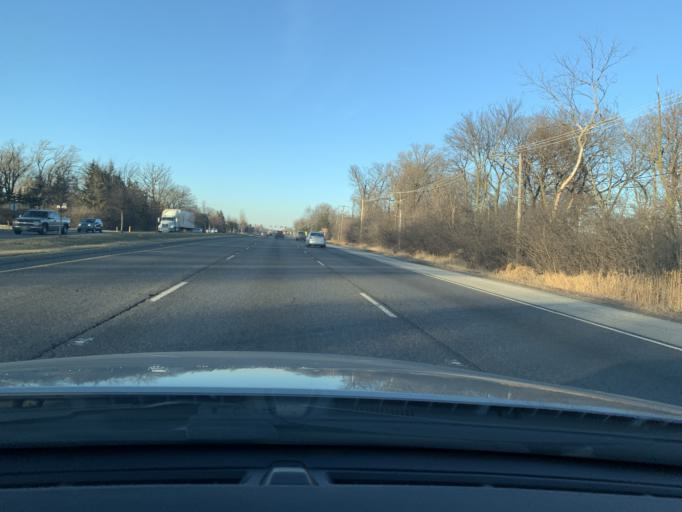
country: US
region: Illinois
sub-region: DuPage County
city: Bensenville
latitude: 41.9517
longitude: -87.9593
